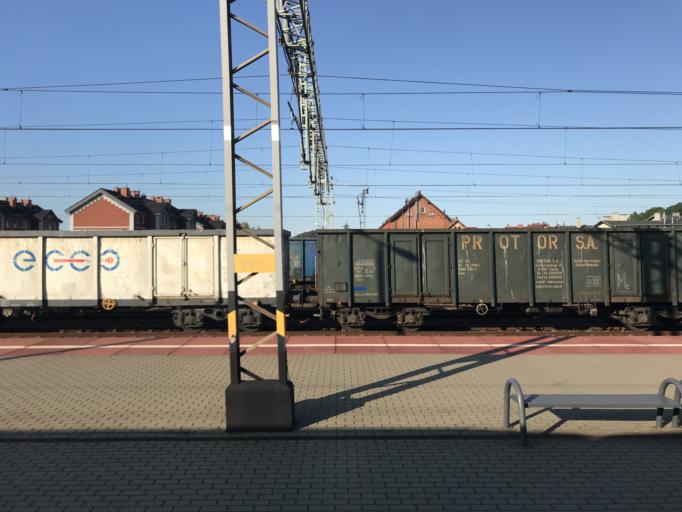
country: PL
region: Pomeranian Voivodeship
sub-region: Powiat tczewski
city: Tczew
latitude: 54.0983
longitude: 18.7892
